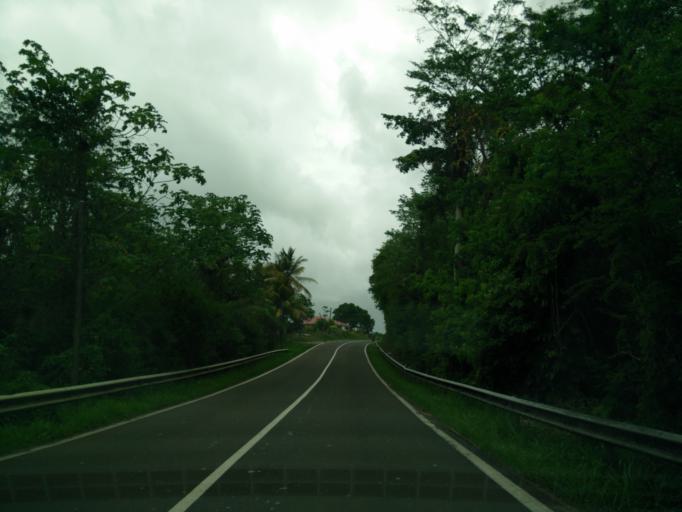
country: GP
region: Guadeloupe
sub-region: Guadeloupe
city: Grand-Bourg
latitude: 15.9074
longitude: -61.2723
